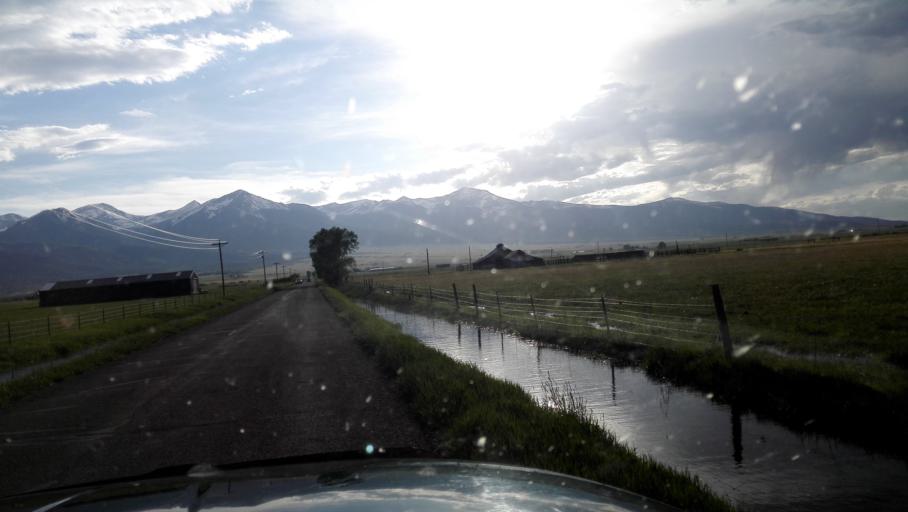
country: US
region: Colorado
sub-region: Custer County
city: Westcliffe
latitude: 38.1317
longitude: -105.4956
